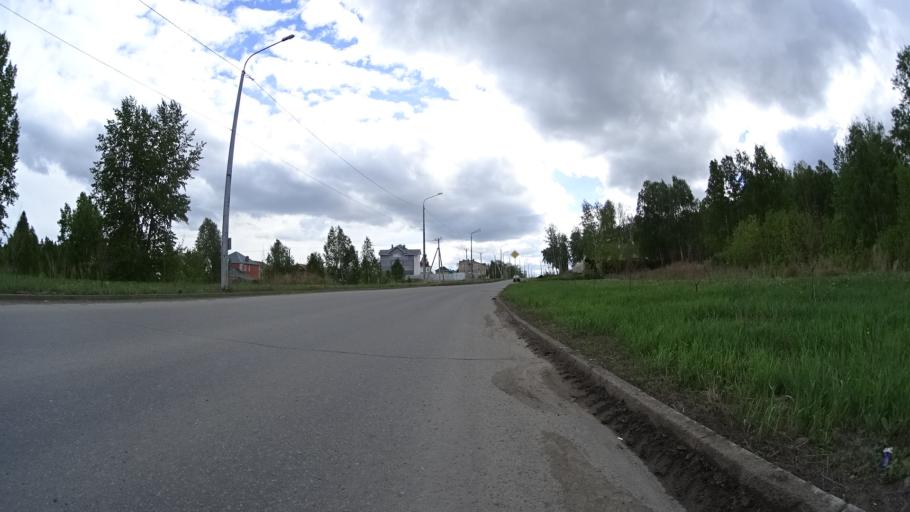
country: RU
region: Chelyabinsk
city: Sargazy
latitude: 55.1575
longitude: 61.2845
